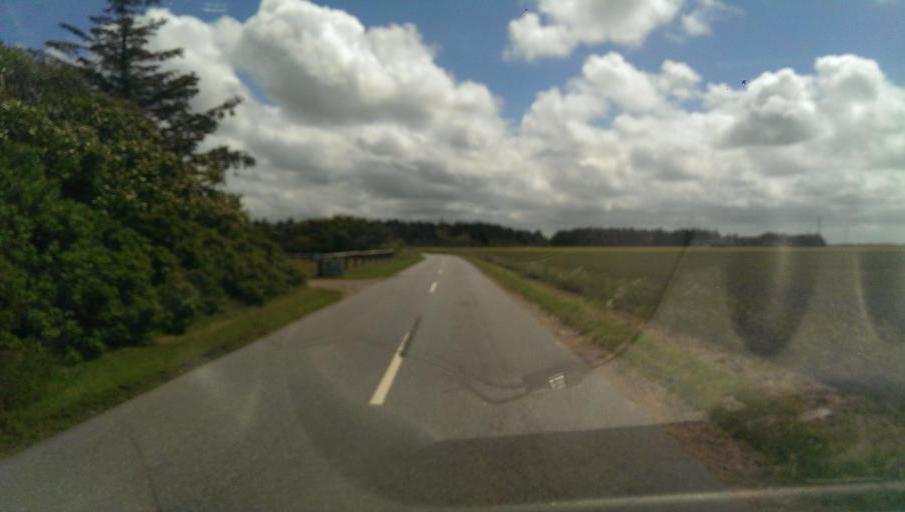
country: DK
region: Central Jutland
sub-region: Holstebro Kommune
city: Ulfborg
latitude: 56.2518
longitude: 8.1730
